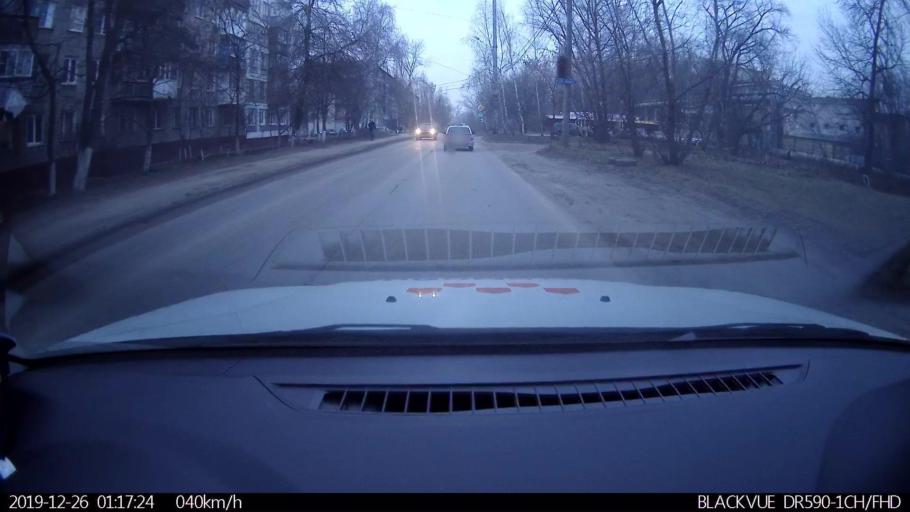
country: RU
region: Nizjnij Novgorod
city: Nizhniy Novgorod
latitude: 56.2682
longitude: 43.8982
